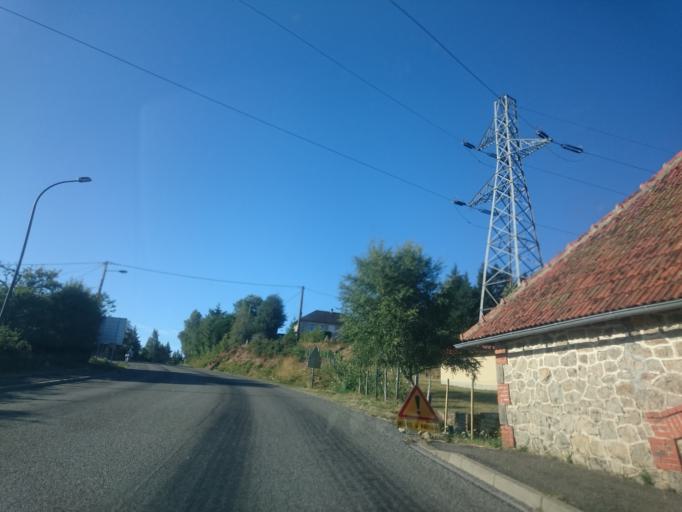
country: FR
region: Midi-Pyrenees
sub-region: Departement de l'Aveyron
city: Entraygues-sur-Truyere
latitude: 44.7118
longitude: 2.5022
